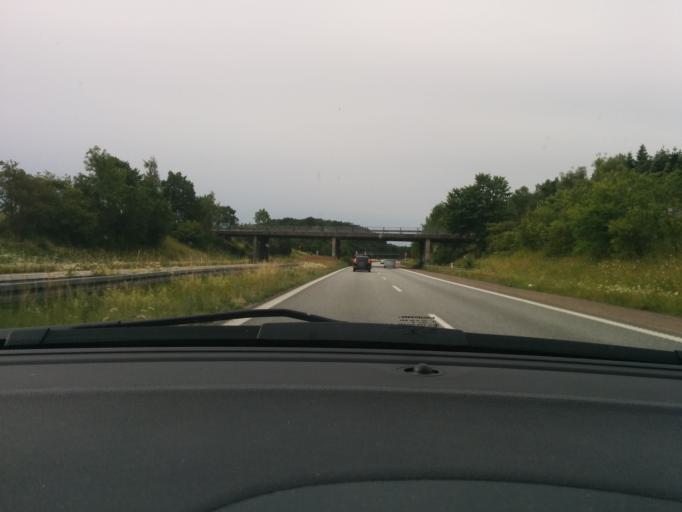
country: DK
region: Zealand
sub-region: Koge Kommune
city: Bjaeverskov
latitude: 55.3843
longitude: 12.0942
